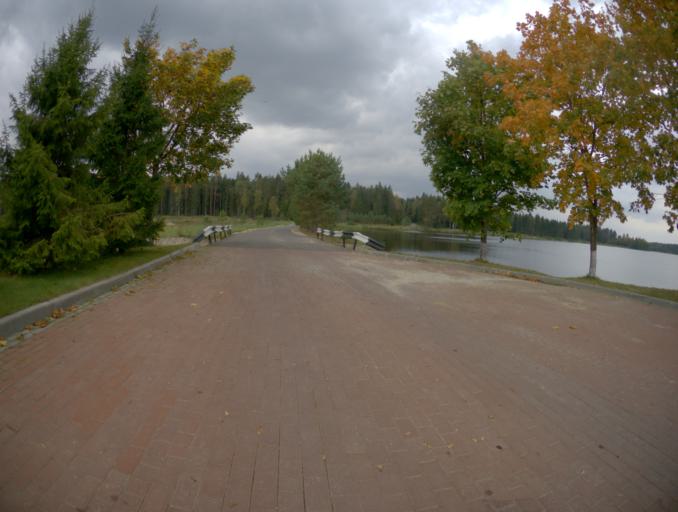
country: RU
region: Vladimir
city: Kideksha
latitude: 56.4734
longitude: 40.6718
